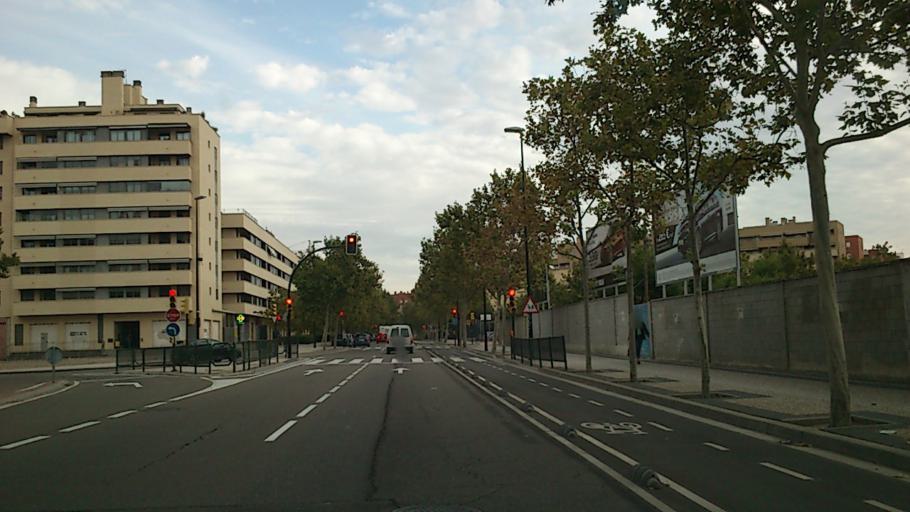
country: ES
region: Aragon
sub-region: Provincia de Zaragoza
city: Zaragoza
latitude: 41.6584
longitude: -0.8689
